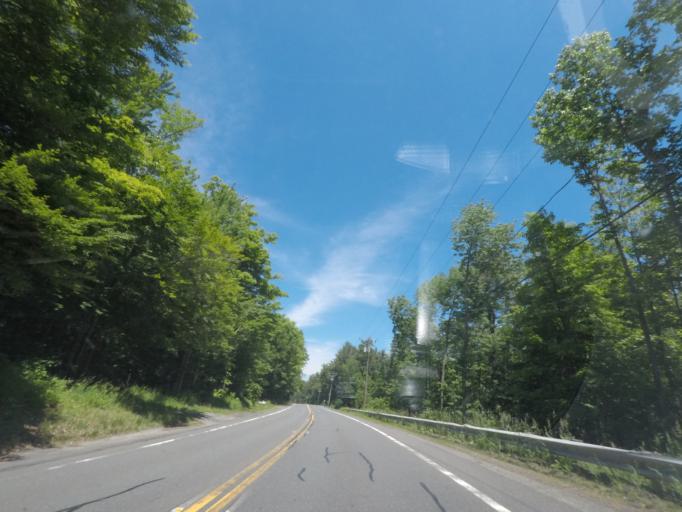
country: US
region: Massachusetts
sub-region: Berkshire County
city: Otis
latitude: 42.2537
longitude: -73.1106
